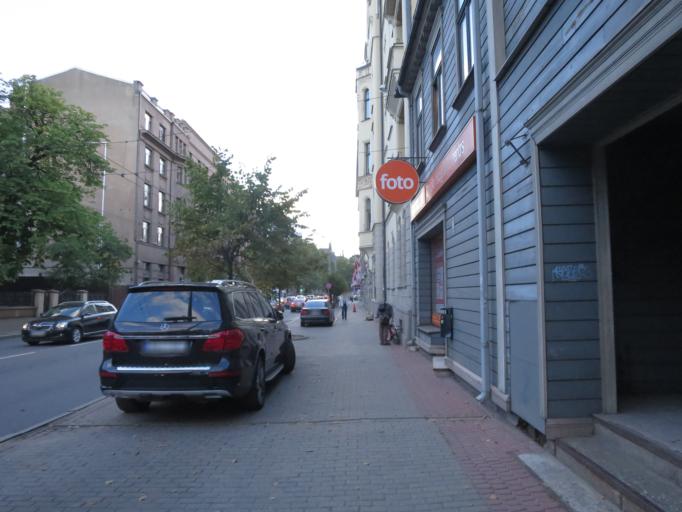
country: LV
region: Riga
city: Riga
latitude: 56.9573
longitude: 24.1151
